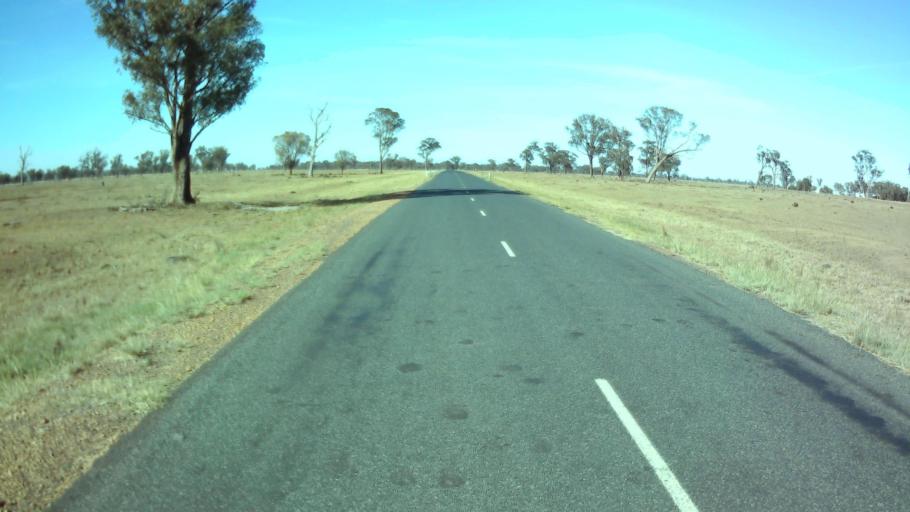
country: AU
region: New South Wales
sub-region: Weddin
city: Grenfell
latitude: -34.0454
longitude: 147.9250
